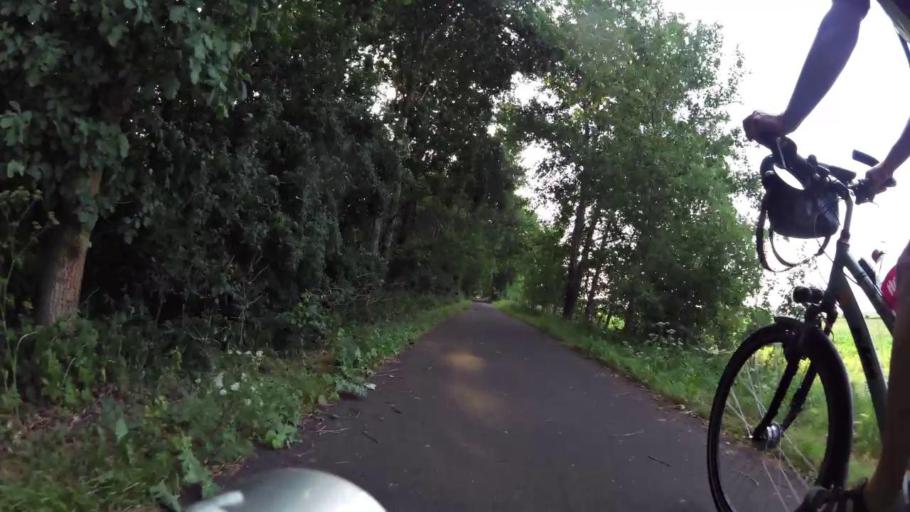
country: PL
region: Kujawsko-Pomorskie
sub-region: Powiat chelminski
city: Unislaw
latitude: 53.1833
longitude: 18.3920
